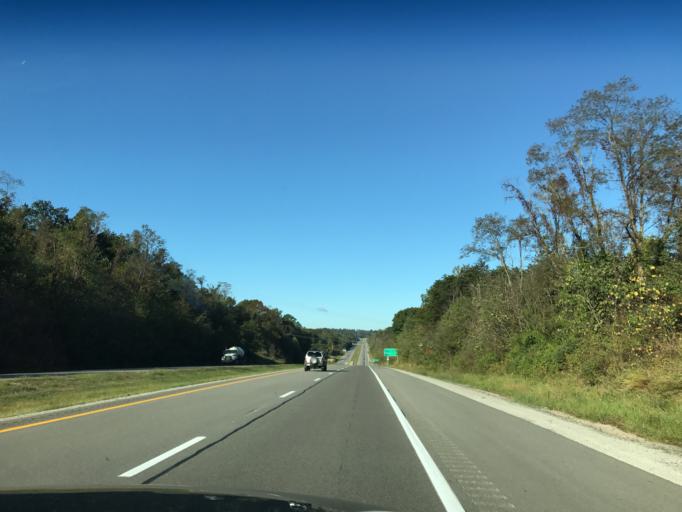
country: US
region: West Virginia
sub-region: Wood County
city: Mineral Wells
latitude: 39.2421
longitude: -81.4190
